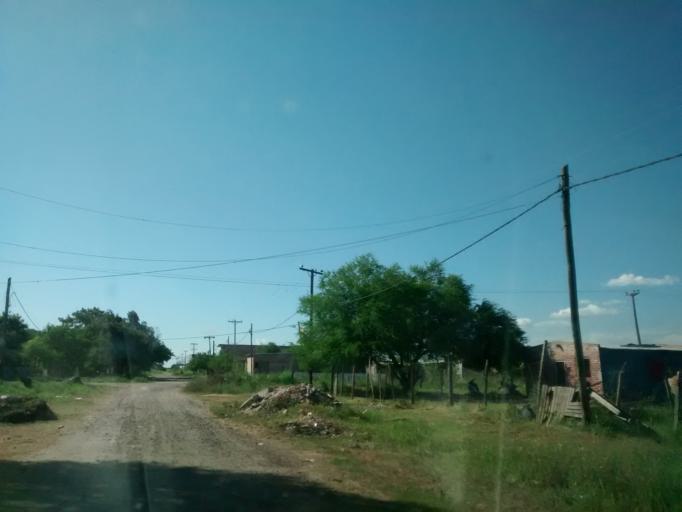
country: AR
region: Chaco
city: Fontana
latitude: -27.4589
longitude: -59.0462
